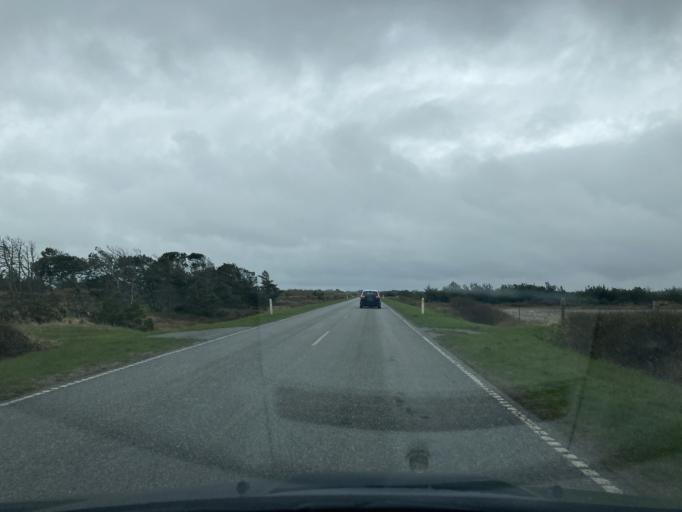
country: DK
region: North Denmark
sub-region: Thisted Kommune
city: Hurup
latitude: 56.9327
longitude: 8.3816
